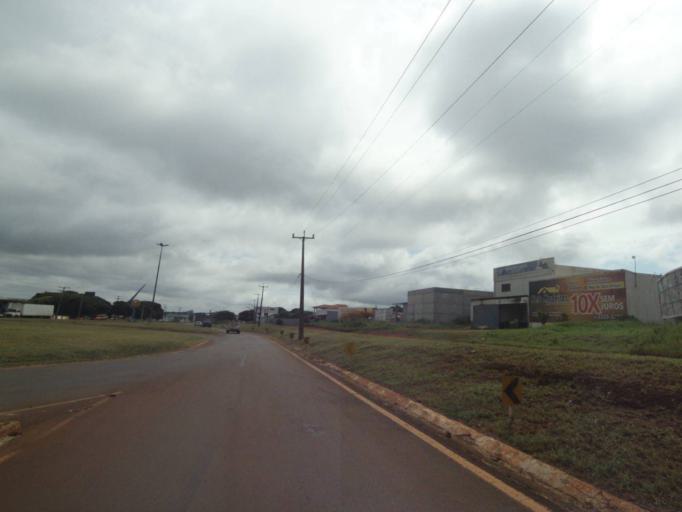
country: BR
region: Parana
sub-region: Campo Mourao
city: Campo Mourao
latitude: -24.0203
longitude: -52.3635
